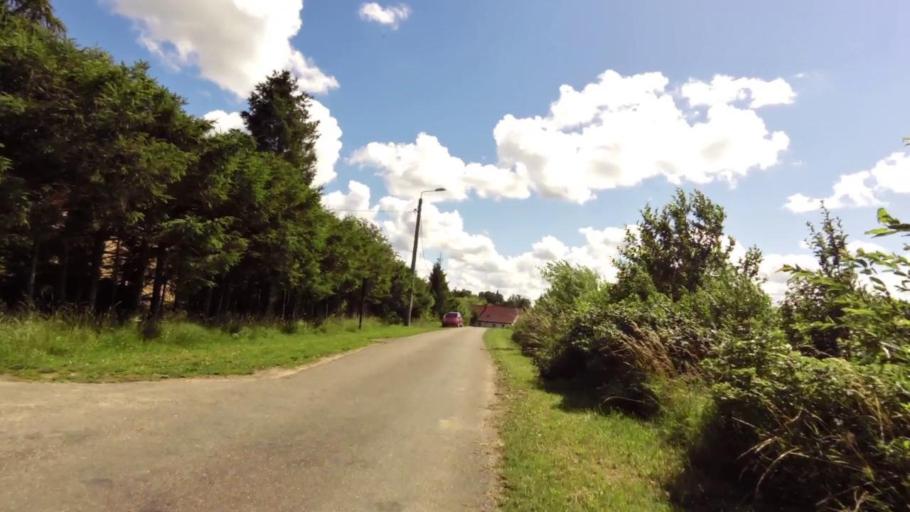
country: PL
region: West Pomeranian Voivodeship
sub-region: Powiat slawienski
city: Slawno
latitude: 54.5250
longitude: 16.6077
